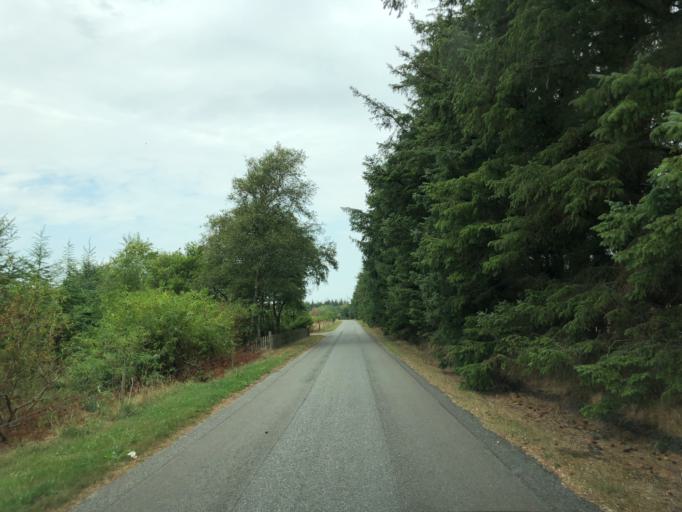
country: DK
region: Central Jutland
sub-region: Holstebro Kommune
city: Ulfborg
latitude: 56.2213
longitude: 8.3230
